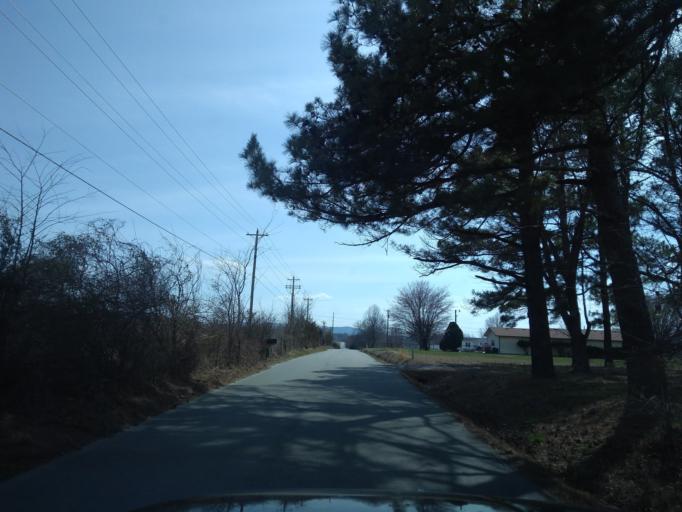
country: US
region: Arkansas
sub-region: Washington County
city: Farmington
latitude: 36.0671
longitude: -94.2401
